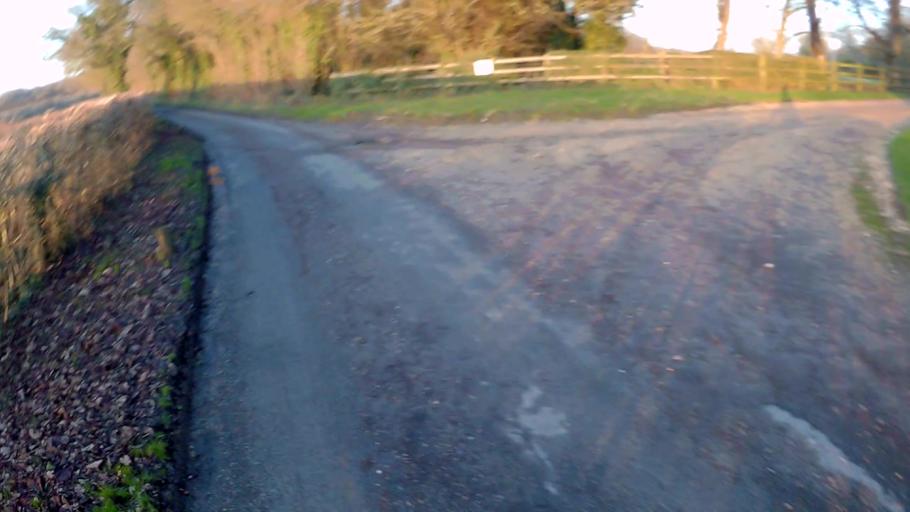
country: GB
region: England
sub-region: Hampshire
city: Overton
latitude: 51.2090
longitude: -1.2446
